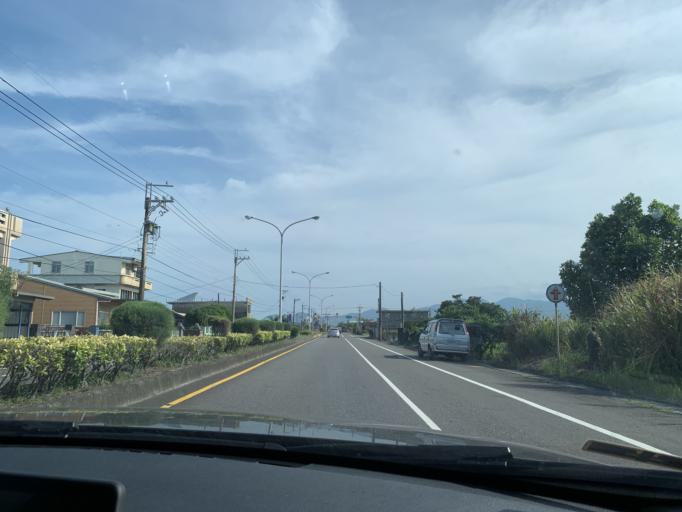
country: TW
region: Taiwan
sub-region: Yilan
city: Yilan
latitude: 24.7451
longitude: 121.8164
